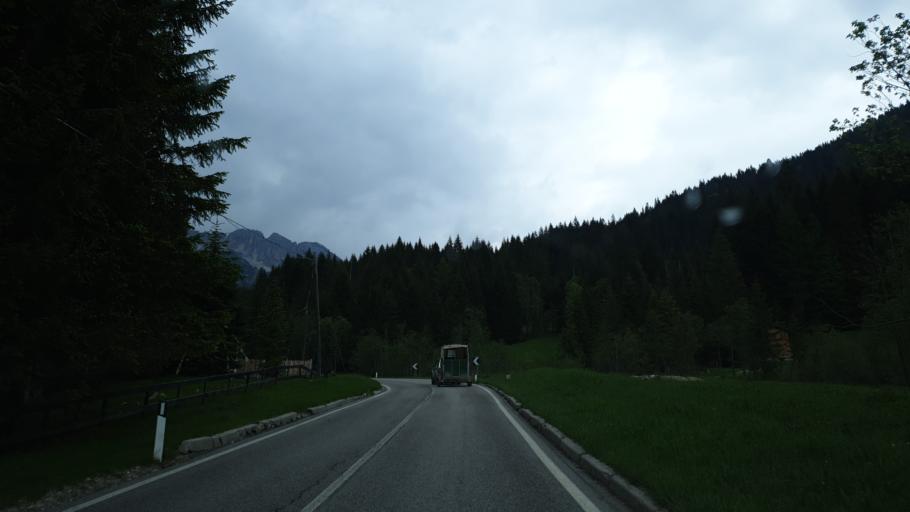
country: IT
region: Veneto
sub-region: Provincia di Belluno
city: San Vito
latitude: 46.5500
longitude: 12.2477
